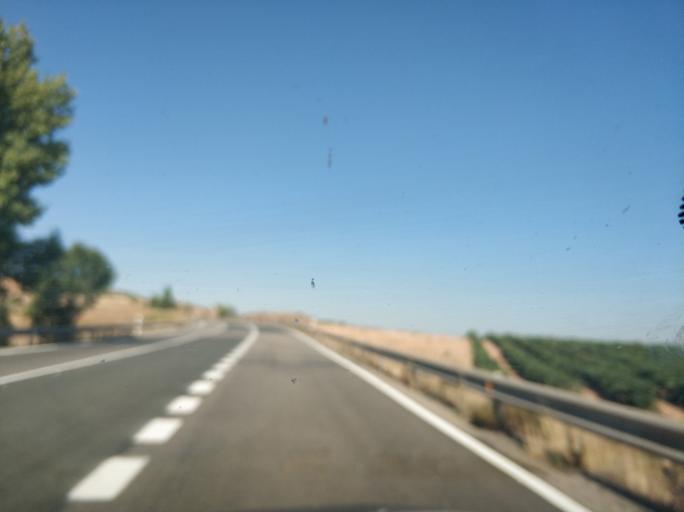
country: ES
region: Castille and Leon
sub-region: Provincia de Burgos
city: Fuentecen
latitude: 41.6322
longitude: -3.8654
